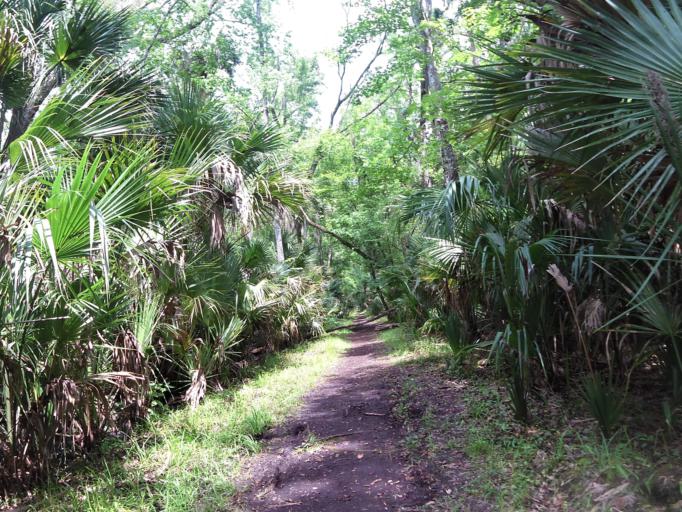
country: US
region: Florida
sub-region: Flagler County
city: Flagler Beach
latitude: 29.3977
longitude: -81.1303
